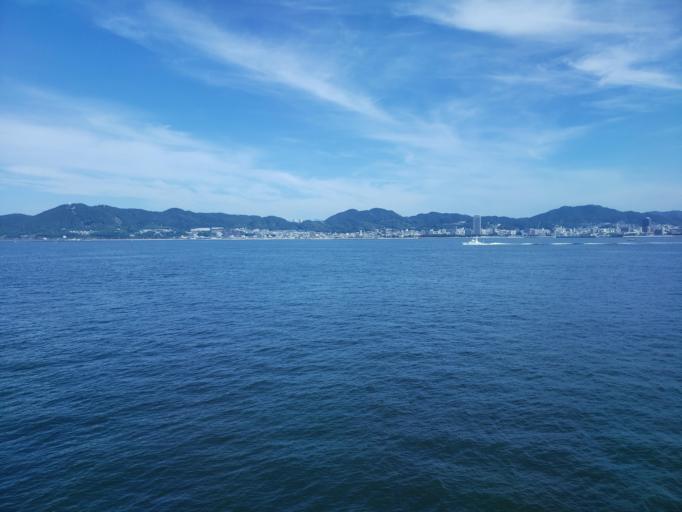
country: JP
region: Hyogo
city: Kobe
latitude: 34.6185
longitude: 135.1320
